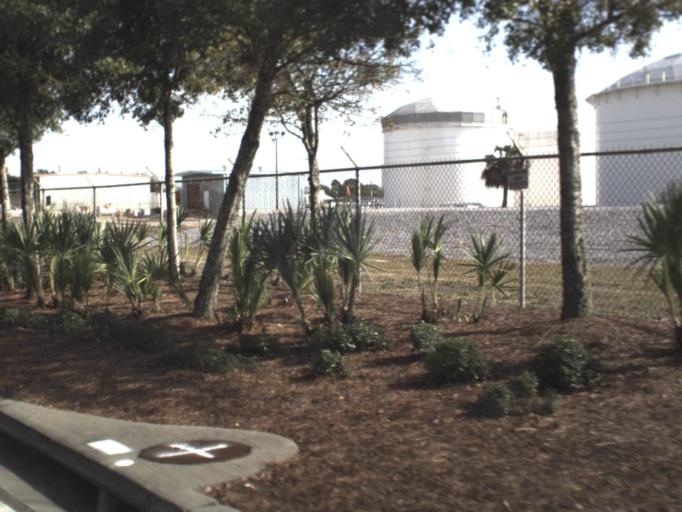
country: US
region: Florida
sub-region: Bay County
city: Panama City
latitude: 30.1595
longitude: -85.6680
